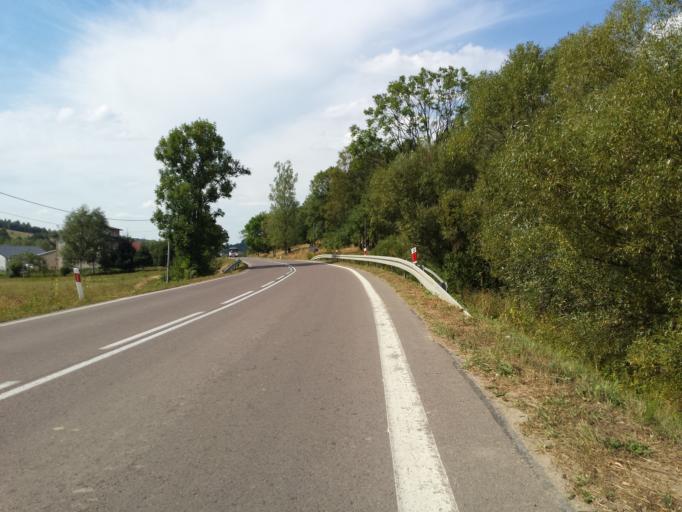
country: PL
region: Subcarpathian Voivodeship
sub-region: Powiat bieszczadzki
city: Ustrzyki Dolne
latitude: 49.5458
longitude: 22.5839
